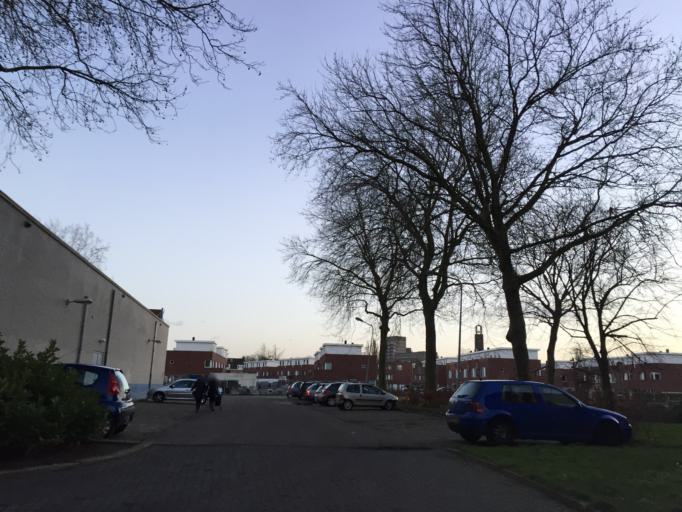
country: NL
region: South Holland
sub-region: Gemeente Lansingerland
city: Berkel en Rodenrijs
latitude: 51.9612
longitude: 4.4663
